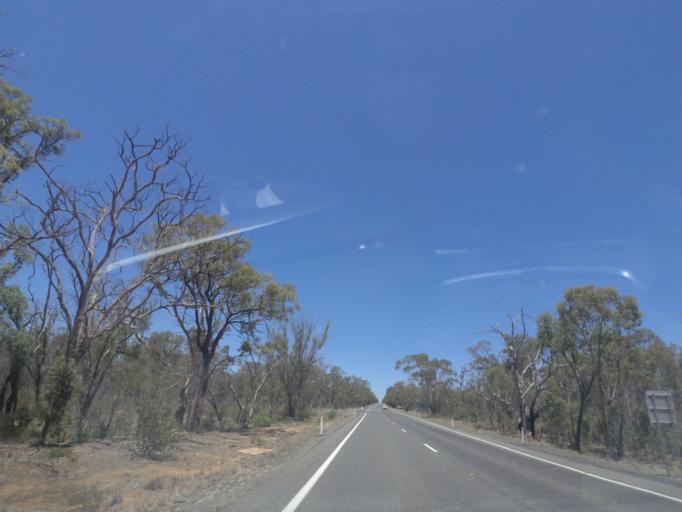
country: AU
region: New South Wales
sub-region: Narrabri
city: Narrabri
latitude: -30.7215
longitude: 149.5252
